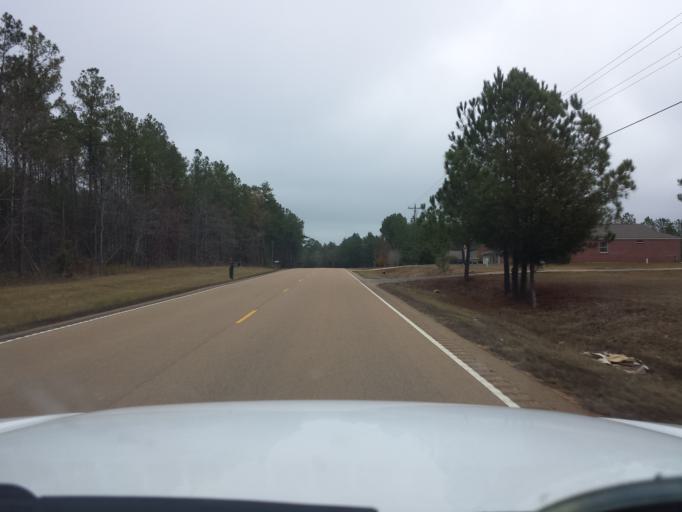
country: US
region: Mississippi
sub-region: Rankin County
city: Pelahatchie
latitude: 32.4572
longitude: -89.9233
